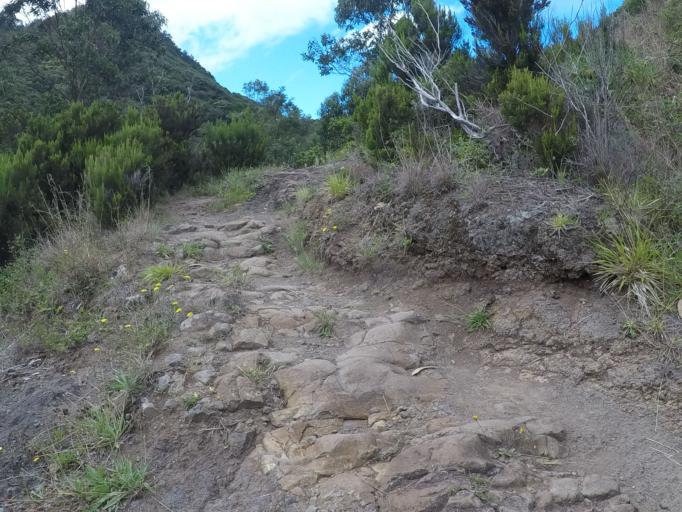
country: PT
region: Madeira
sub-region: Machico
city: Canical
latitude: 32.7527
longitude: -16.7703
